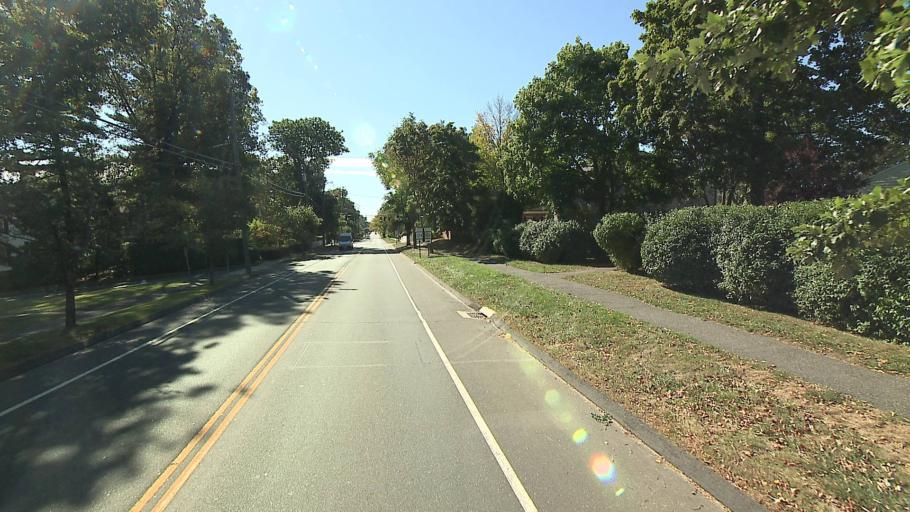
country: US
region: Connecticut
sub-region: Fairfield County
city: New Canaan
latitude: 41.1404
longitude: -73.4911
